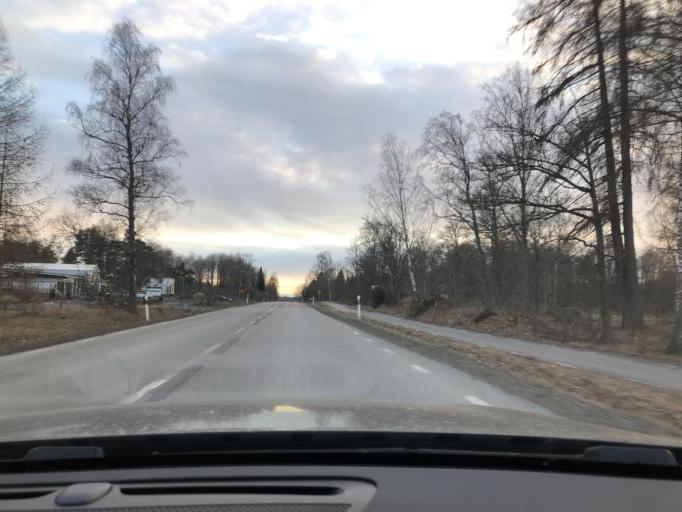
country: SE
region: Uppsala
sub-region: Uppsala Kommun
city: Gamla Uppsala
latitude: 59.9372
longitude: 17.6483
